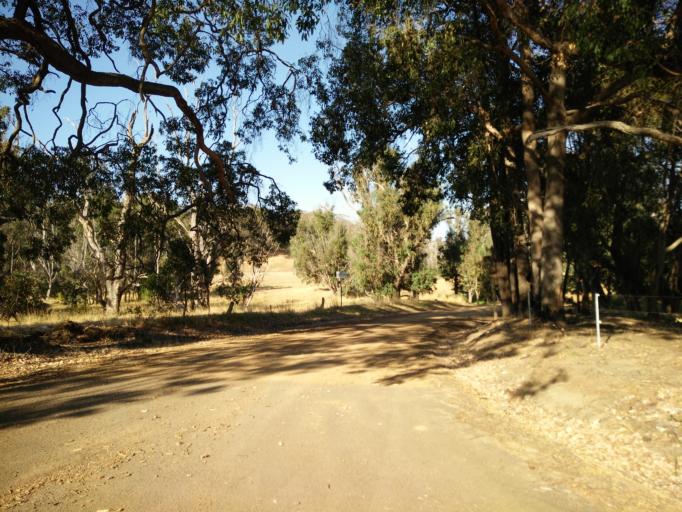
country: AU
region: Western Australia
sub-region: Donnybrook-Balingup
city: Donnybrook
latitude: -33.6679
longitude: 115.8035
